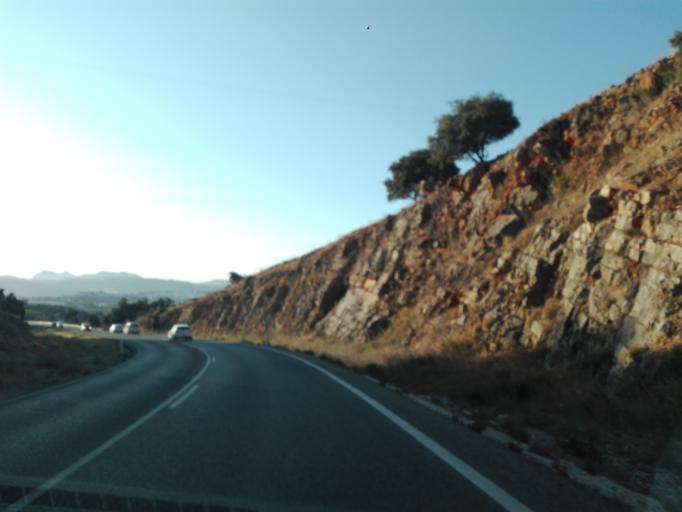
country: ES
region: Andalusia
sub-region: Provincia de Malaga
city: Ronda
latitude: 36.7118
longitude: -5.1310
